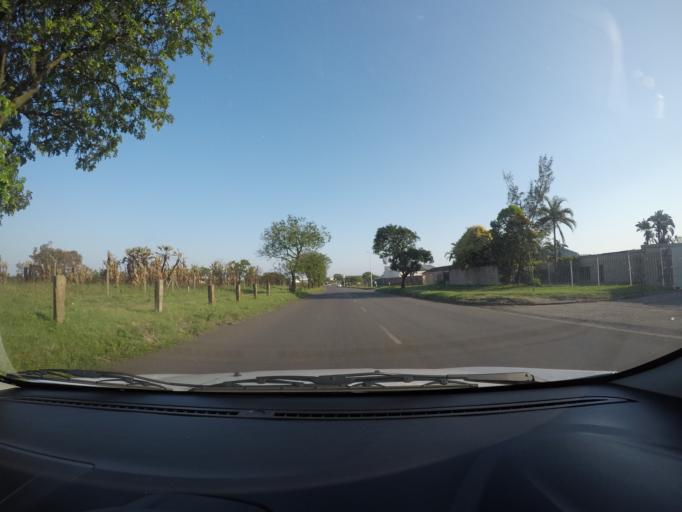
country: ZA
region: KwaZulu-Natal
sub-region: uThungulu District Municipality
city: Richards Bay
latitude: -28.7641
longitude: 32.0078
